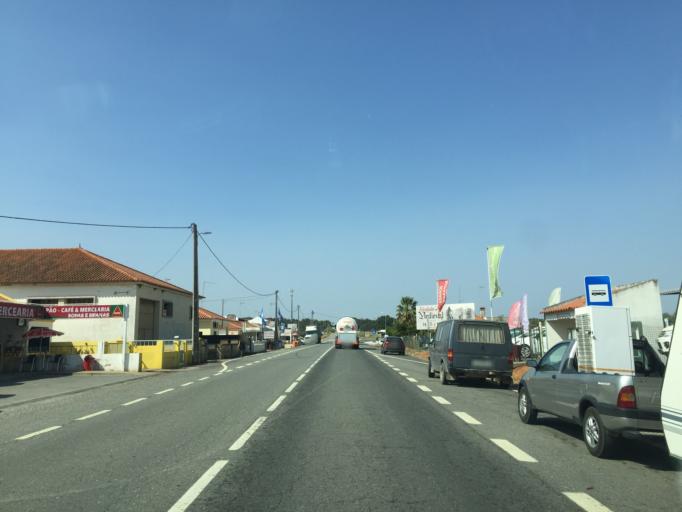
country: PT
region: Beja
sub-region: Aljustrel
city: Aljustrel
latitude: 37.9471
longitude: -8.3807
